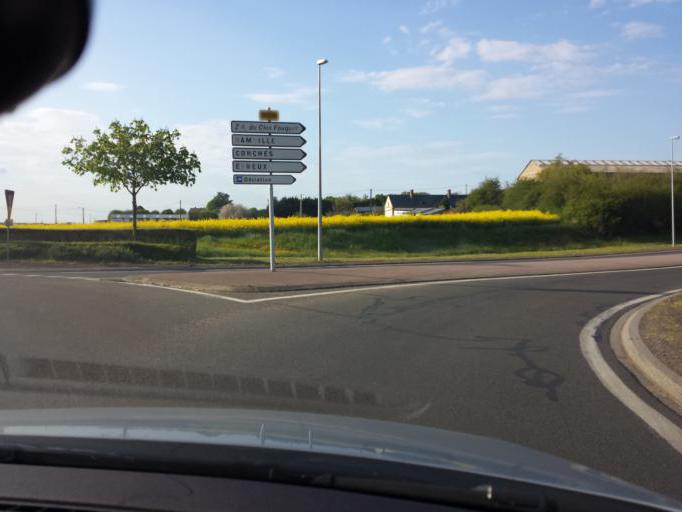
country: FR
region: Haute-Normandie
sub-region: Departement de l'Eure
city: Breteuil
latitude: 48.8186
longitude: 0.9217
